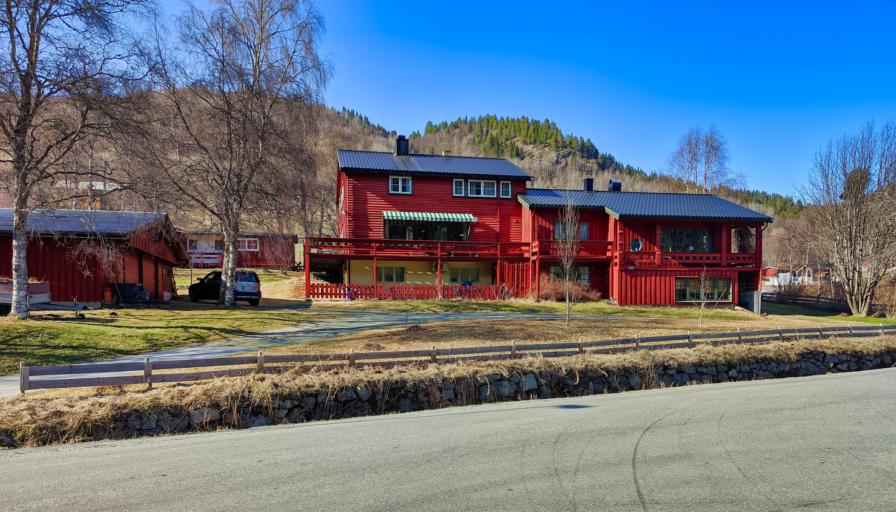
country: NO
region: Aust-Agder
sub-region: Bykle
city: Hovden
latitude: 59.7370
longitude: 7.5640
